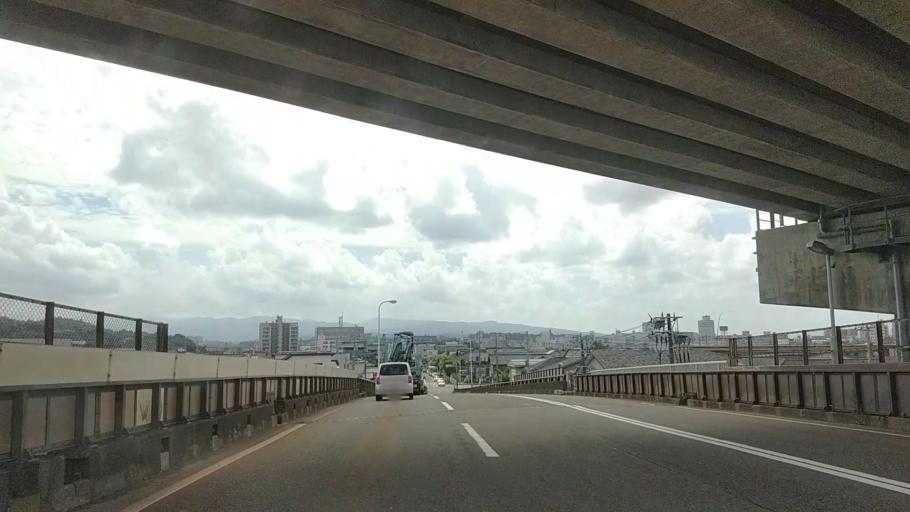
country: JP
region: Ishikawa
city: Kanazawa-shi
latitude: 36.5877
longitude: 136.6633
